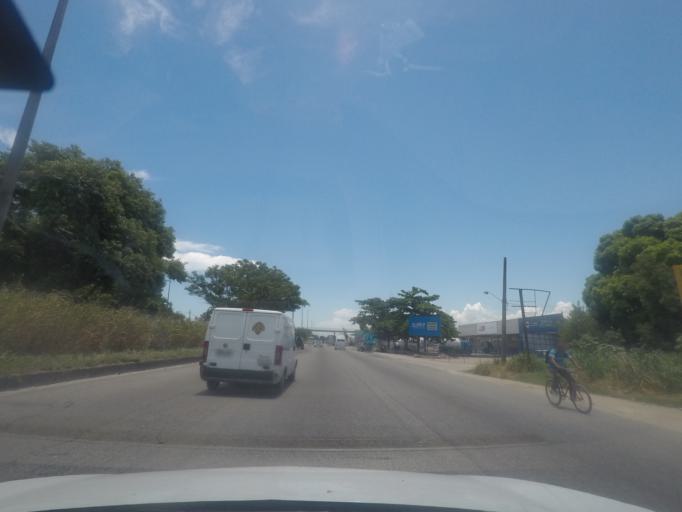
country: BR
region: Rio de Janeiro
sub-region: Itaguai
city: Itaguai
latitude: -22.8910
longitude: -43.6674
